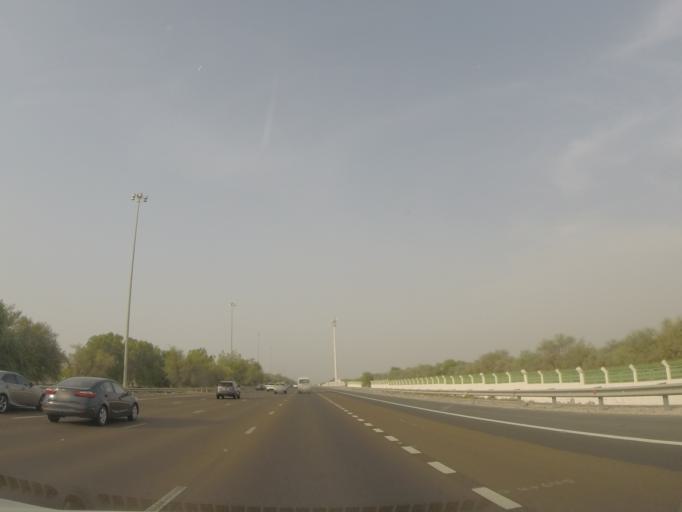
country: AE
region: Abu Dhabi
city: Abu Dhabi
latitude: 24.7105
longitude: 54.7954
